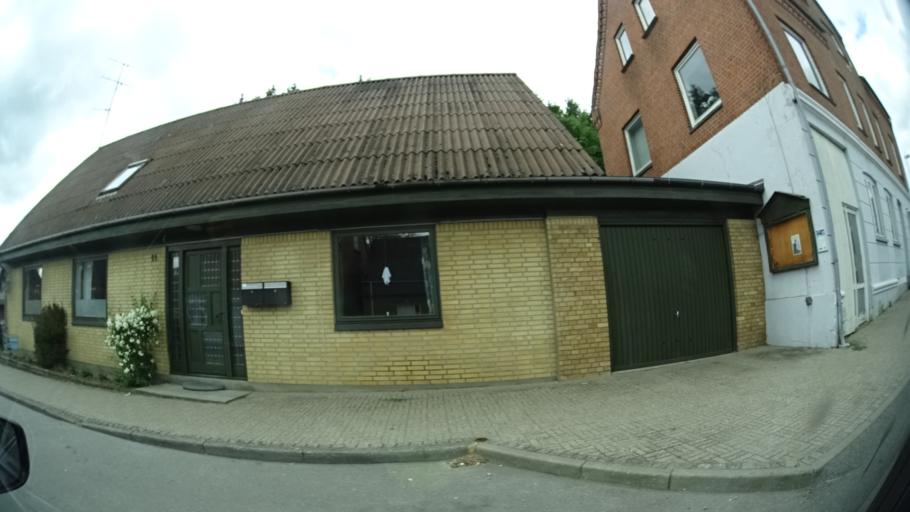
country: DK
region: Central Jutland
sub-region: Syddjurs Kommune
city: Ryomgard
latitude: 56.4087
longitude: 10.5676
